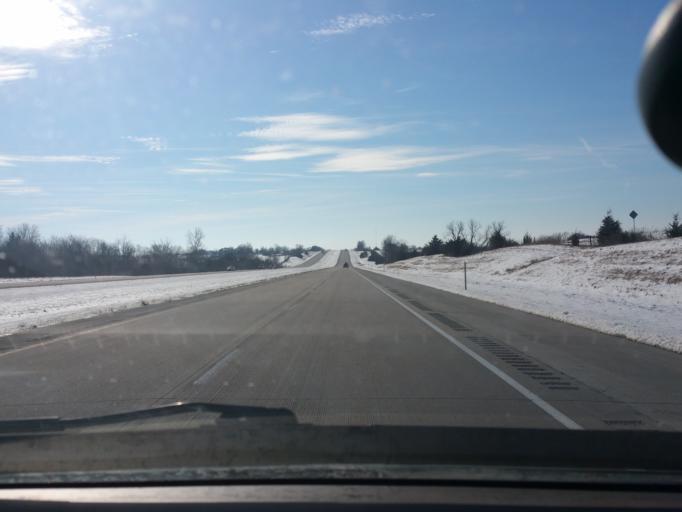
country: US
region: Iowa
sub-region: Decatur County
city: Leon
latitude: 40.7930
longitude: -93.8349
